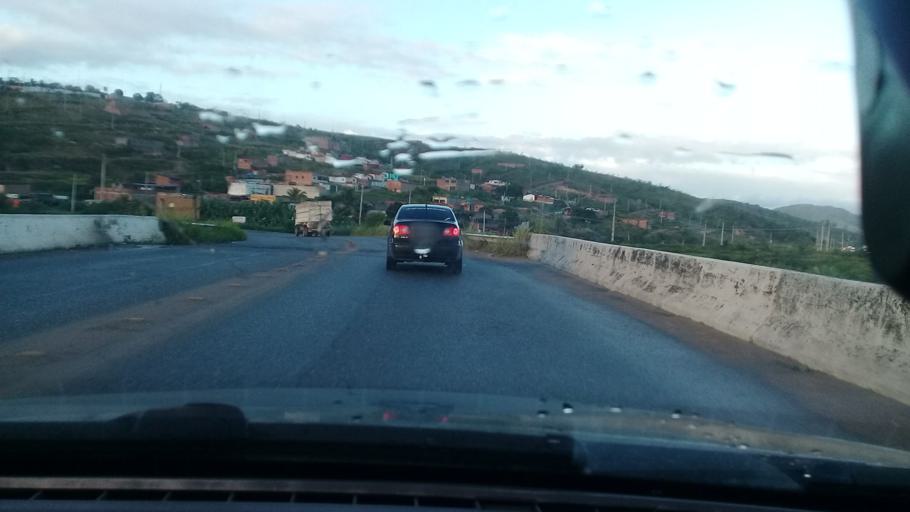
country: BR
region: Pernambuco
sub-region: Vitoria De Santo Antao
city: Vitoria de Santo Antao
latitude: -8.1289
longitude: -35.2821
